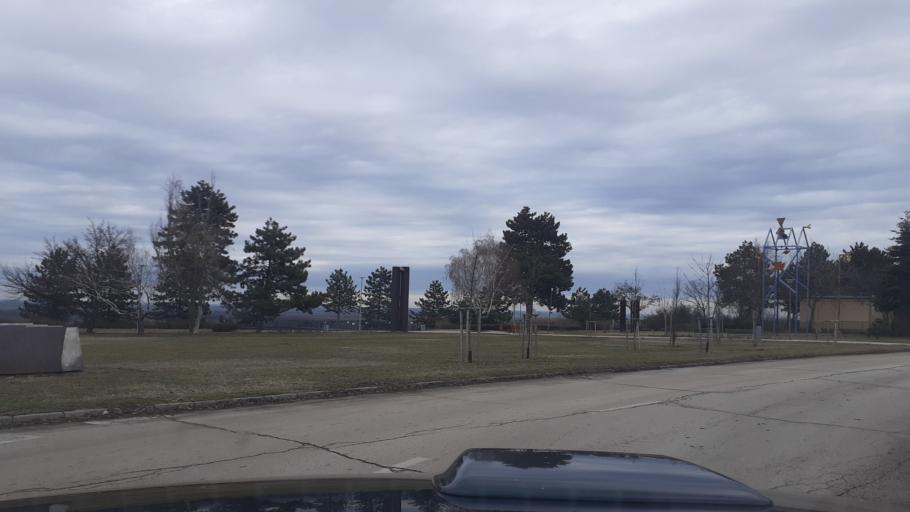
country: HU
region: Fejer
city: Dunaujvaros
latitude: 46.9665
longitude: 18.9434
